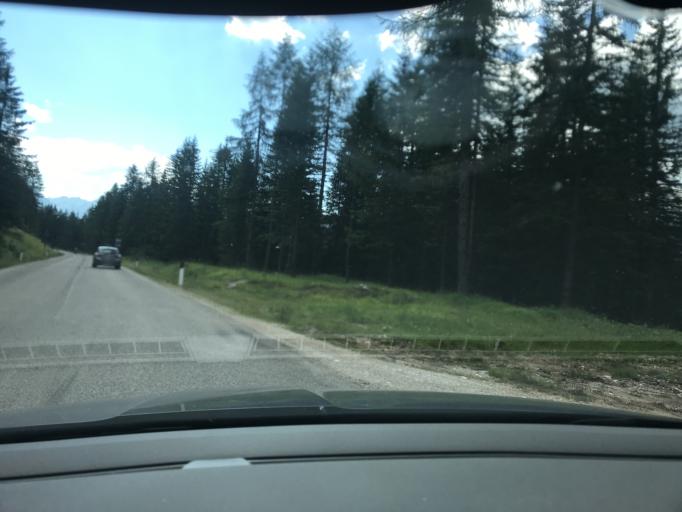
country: IT
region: Veneto
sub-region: Provincia di Belluno
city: Cortina d'Ampezzo
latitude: 46.5210
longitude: 12.0845
